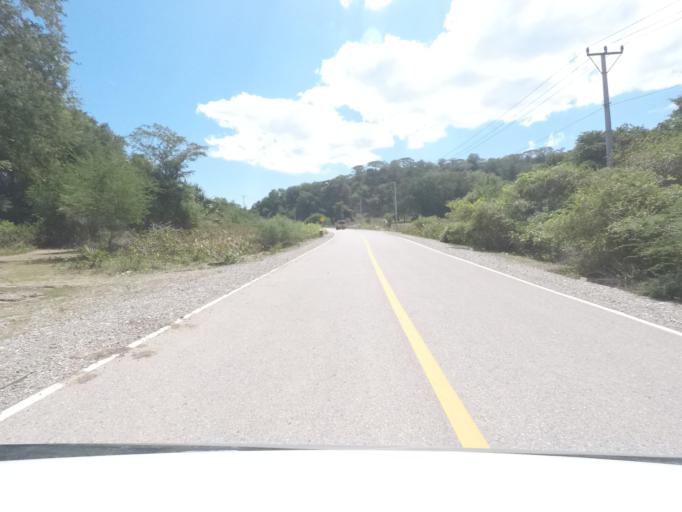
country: TL
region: Lautem
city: Lospalos
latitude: -8.4128
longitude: 126.8093
